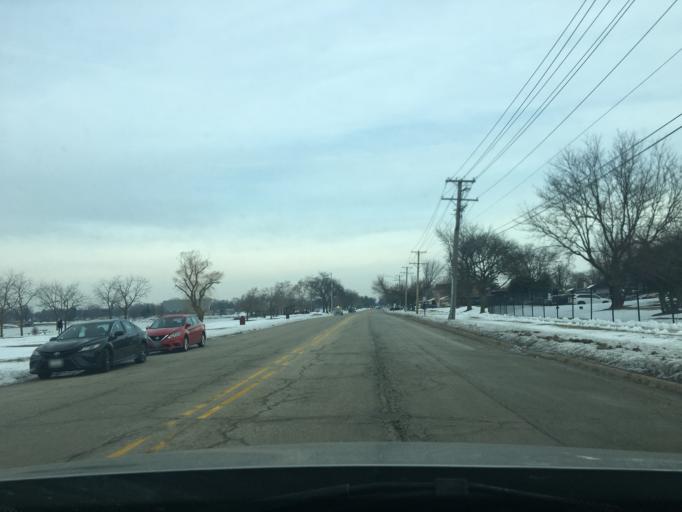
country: US
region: Illinois
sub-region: Cook County
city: Rosemont
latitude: 42.0106
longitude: -87.8942
